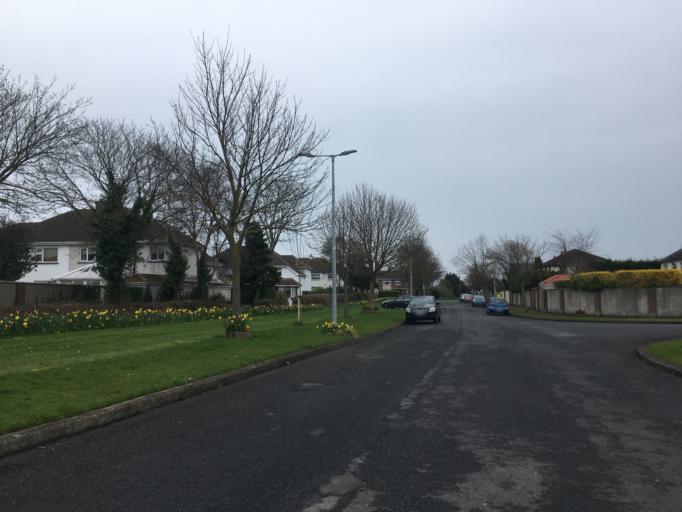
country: IE
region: Leinster
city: Portmarnock
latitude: 53.4240
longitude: -6.1368
